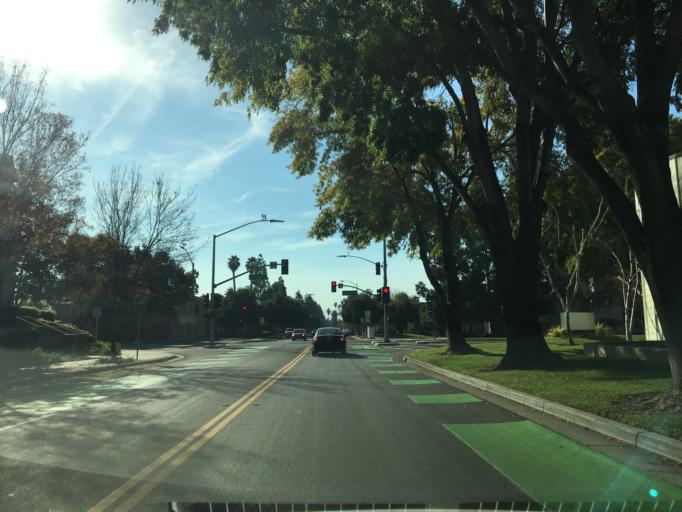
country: US
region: California
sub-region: Santa Clara County
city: Milpitas
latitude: 37.3890
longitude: -121.8934
